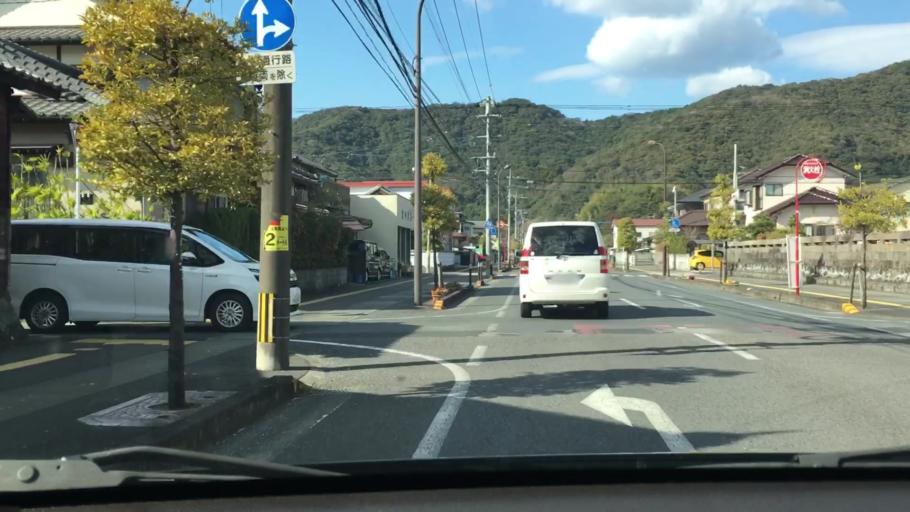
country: JP
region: Oita
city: Saiki
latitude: 32.9623
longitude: 131.8986
